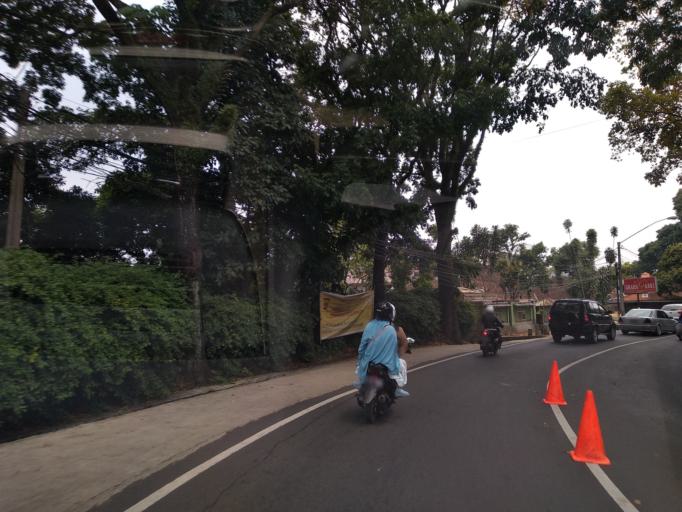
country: ID
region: West Java
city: Lembang
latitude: -6.8493
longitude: 107.5984
